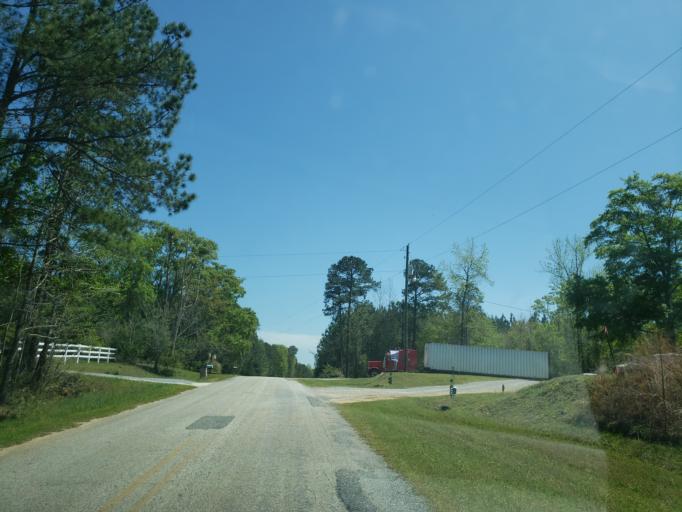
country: US
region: Alabama
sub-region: Tallapoosa County
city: Camp Hill
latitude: 32.6674
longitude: -85.7278
